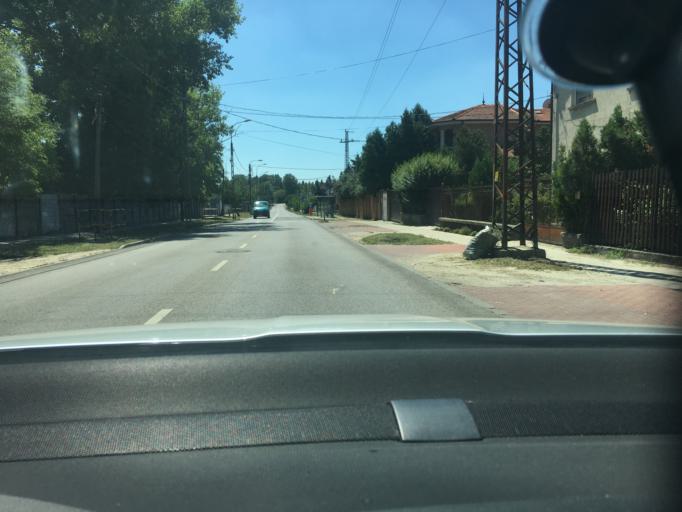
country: HU
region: Pest
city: Csomor
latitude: 47.5180
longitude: 19.2235
